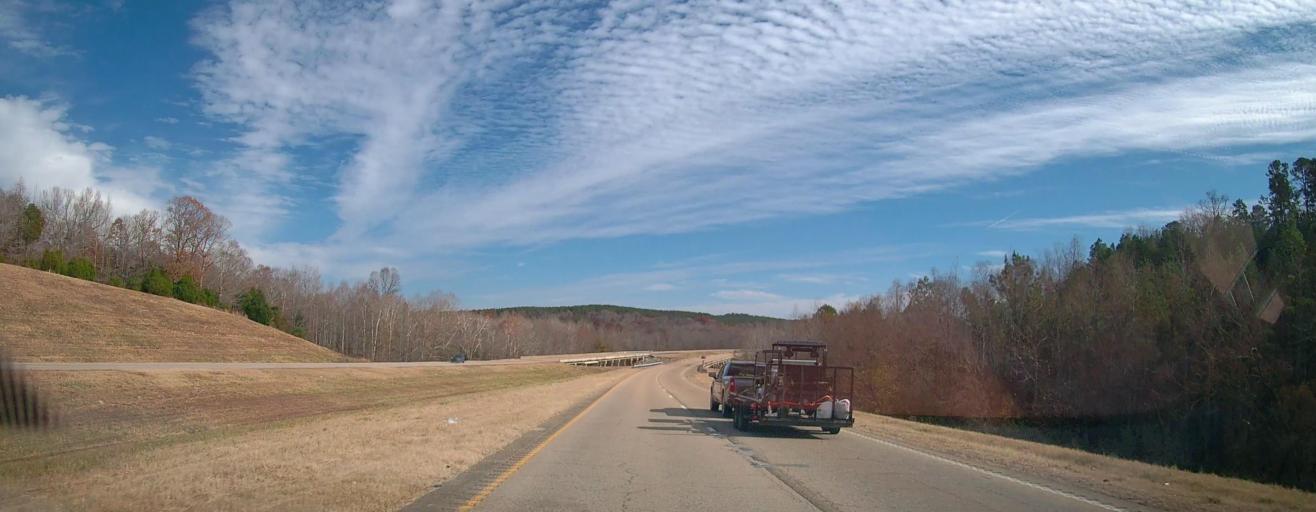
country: US
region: Mississippi
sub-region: Tippah County
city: Ripley
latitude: 34.9459
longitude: -88.7950
